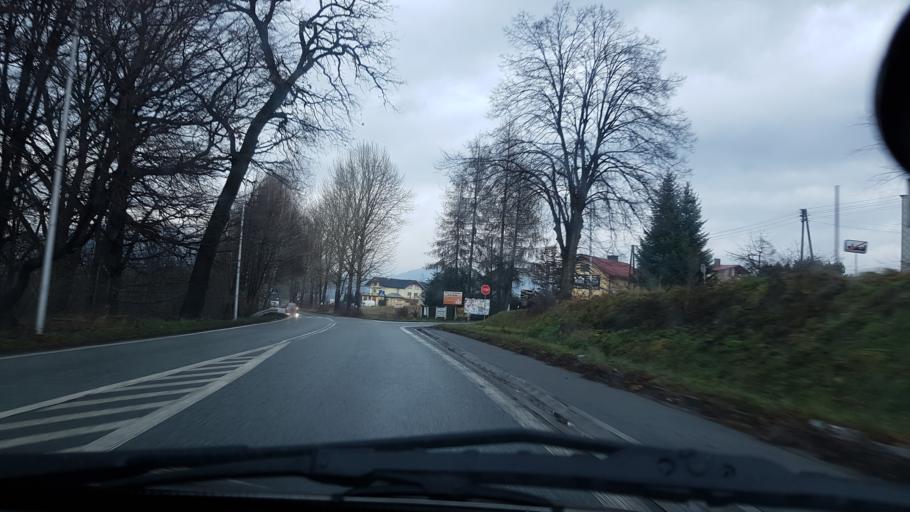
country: PL
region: Silesian Voivodeship
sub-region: Powiat zywiecki
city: Zywiec
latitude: 49.7054
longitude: 19.2074
